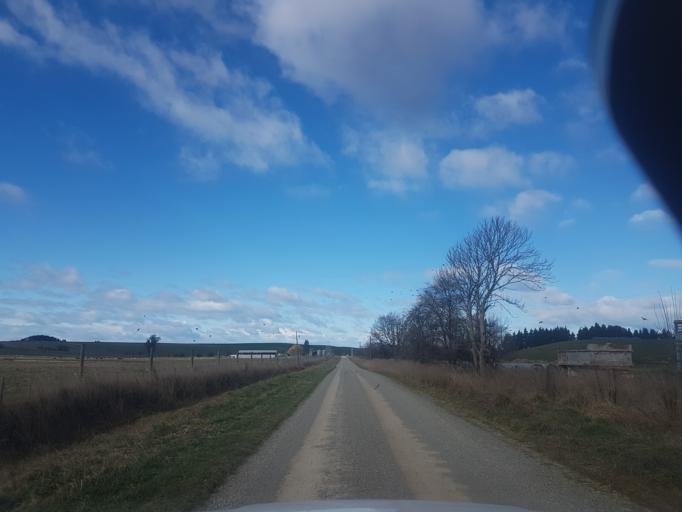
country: NZ
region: Canterbury
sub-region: Timaru District
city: Pleasant Point
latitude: -44.1897
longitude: 171.1964
